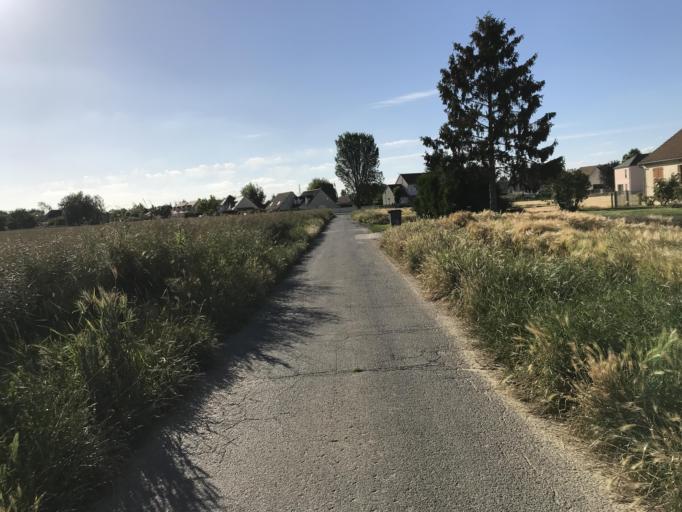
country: FR
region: Ile-de-France
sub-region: Departement de l'Essonne
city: Villejust
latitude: 48.6712
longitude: 2.2192
